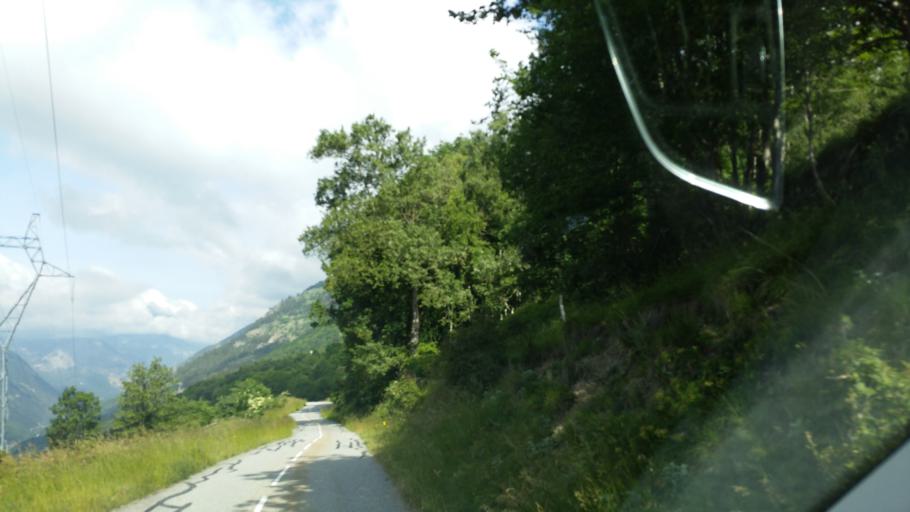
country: FR
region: Rhone-Alpes
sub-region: Departement de la Savoie
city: Modane
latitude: 45.2101
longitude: 6.6069
